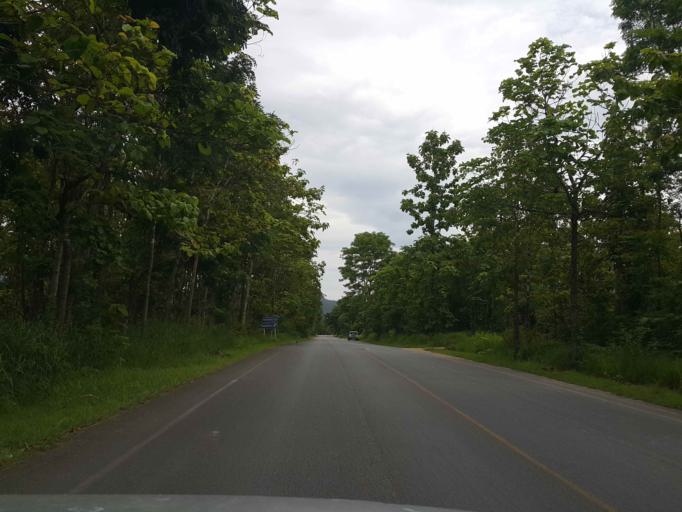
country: TH
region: Lampang
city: Thoen
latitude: 17.5876
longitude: 99.3306
